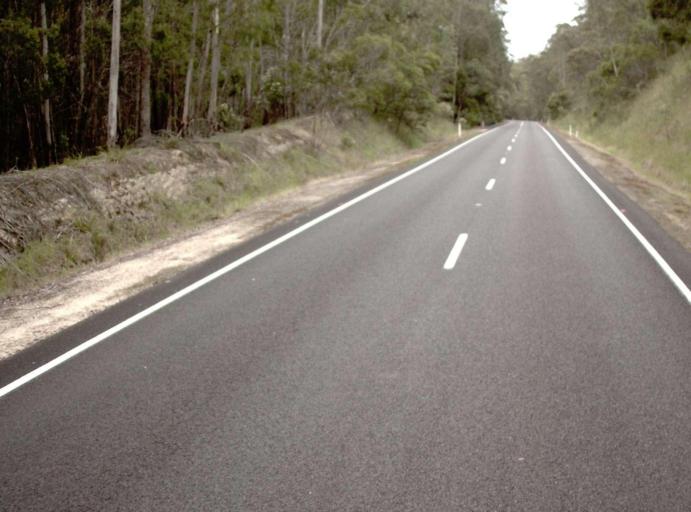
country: AU
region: New South Wales
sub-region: Bombala
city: Bombala
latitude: -37.3042
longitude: 149.2103
